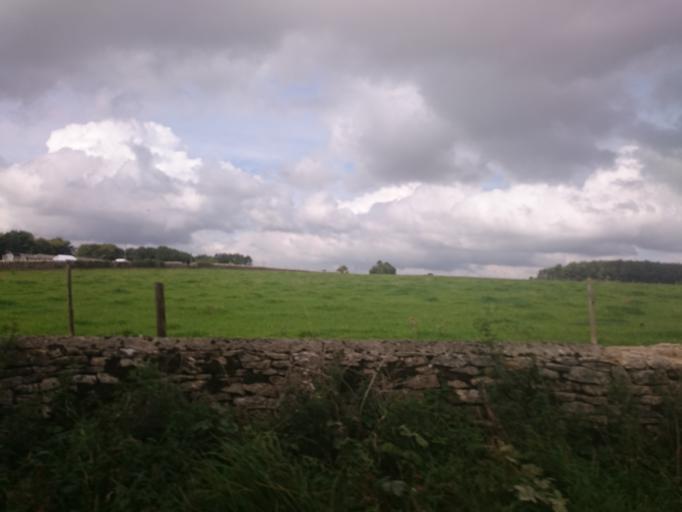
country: GB
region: England
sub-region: Gloucestershire
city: Coates
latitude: 51.7760
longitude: -2.0373
